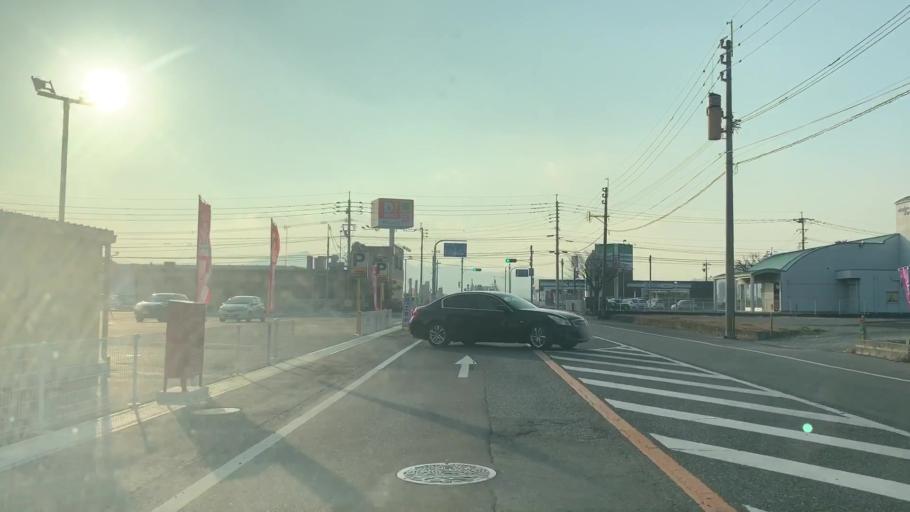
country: JP
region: Saga Prefecture
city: Saga-shi
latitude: 33.2774
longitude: 130.2162
